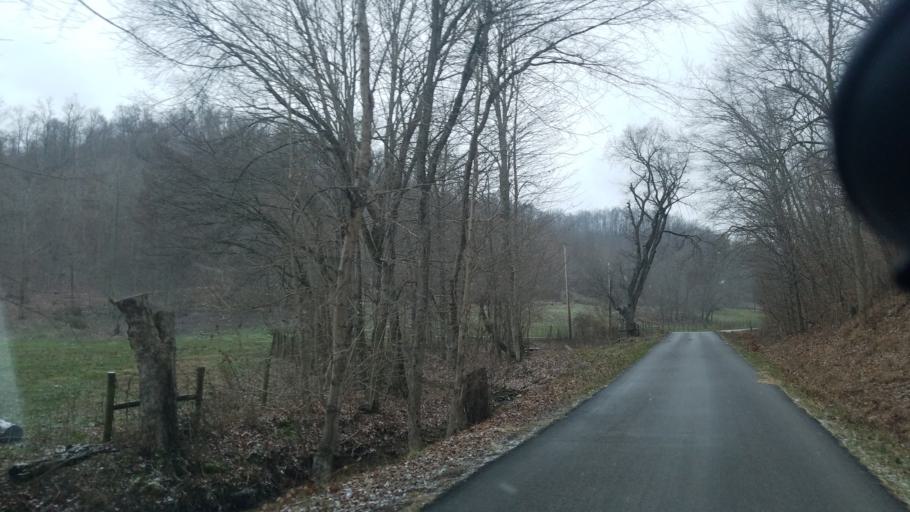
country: US
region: Kentucky
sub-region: Lewis County
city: Vanceburg
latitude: 38.4796
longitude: -83.5003
